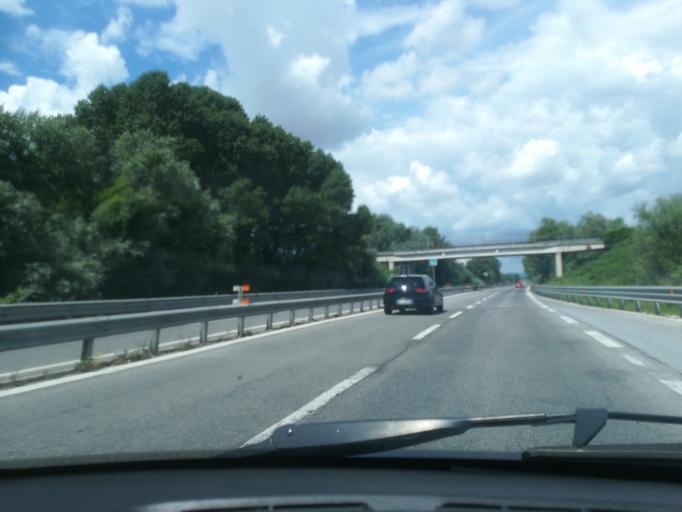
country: IT
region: The Marches
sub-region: Provincia di Macerata
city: Villa San Filippo
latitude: 43.2631
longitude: 13.5581
